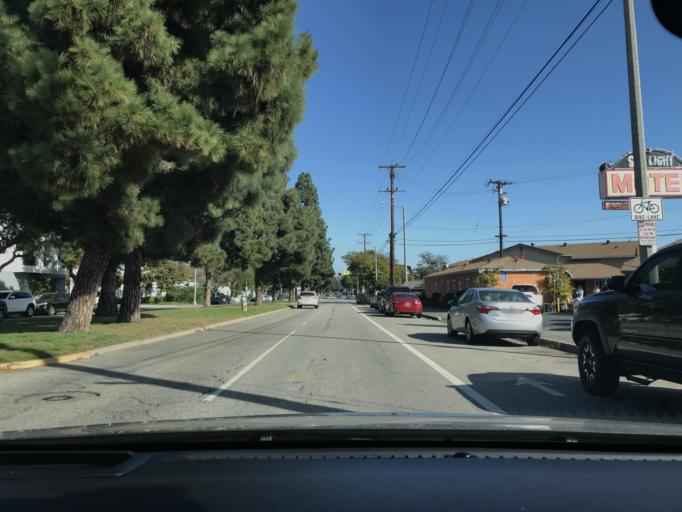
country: US
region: California
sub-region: Los Angeles County
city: Signal Hill
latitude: 33.8352
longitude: -118.1879
